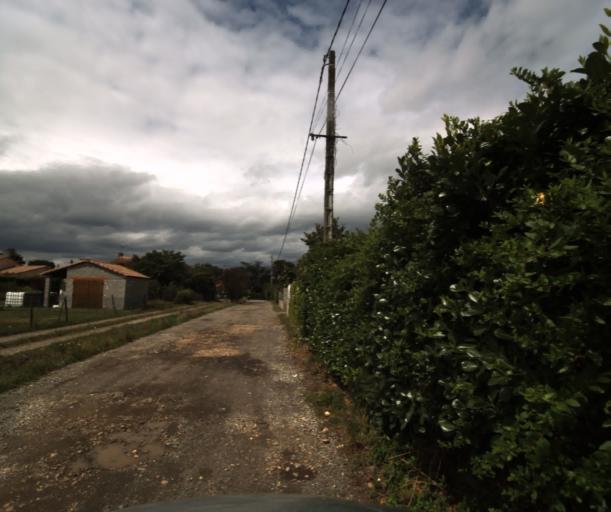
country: FR
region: Midi-Pyrenees
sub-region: Departement de la Haute-Garonne
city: Roquettes
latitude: 43.4767
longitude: 1.3778
